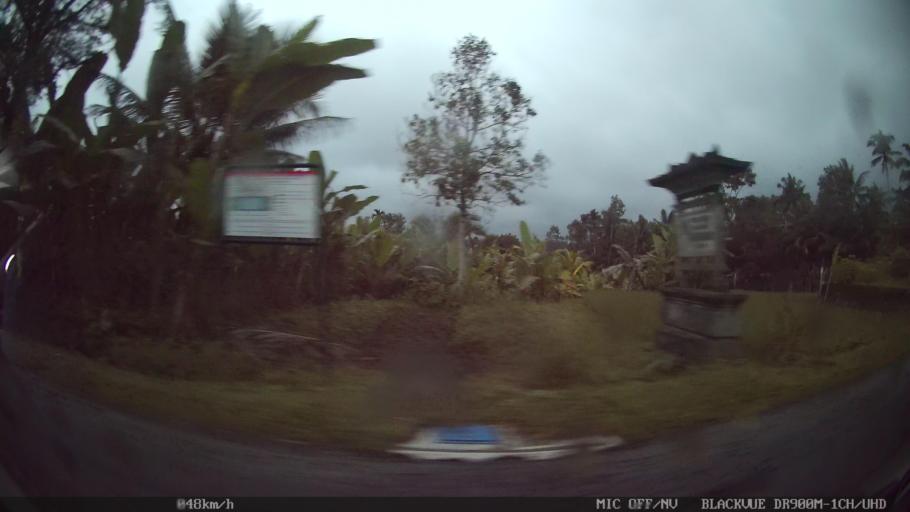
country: ID
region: Bali
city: Banjar Ponggang
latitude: -8.3928
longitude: 115.2563
